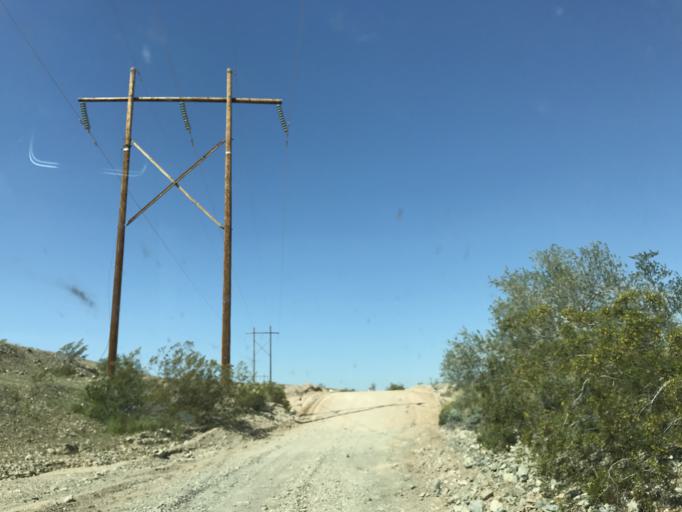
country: US
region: California
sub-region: Riverside County
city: Mesa Verde
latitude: 33.4974
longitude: -114.8436
